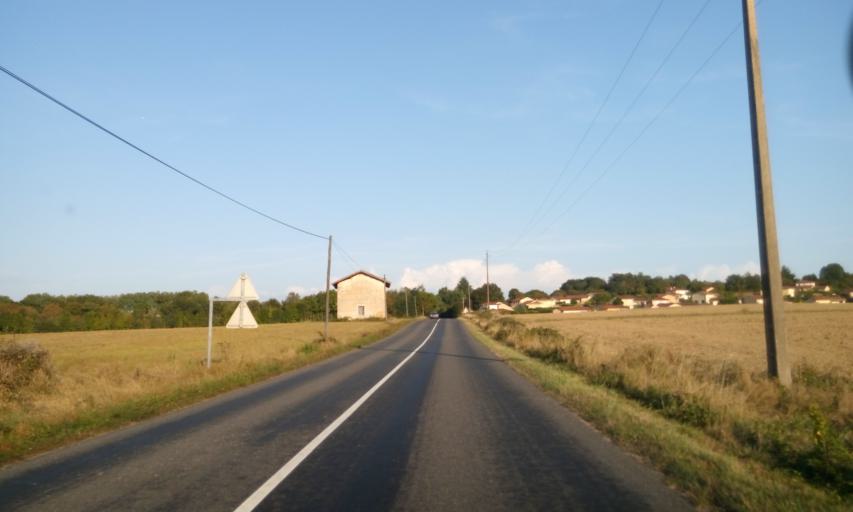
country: FR
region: Rhone-Alpes
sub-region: Departement de l'Ain
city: Chalamont
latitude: 45.9990
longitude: 5.1575
